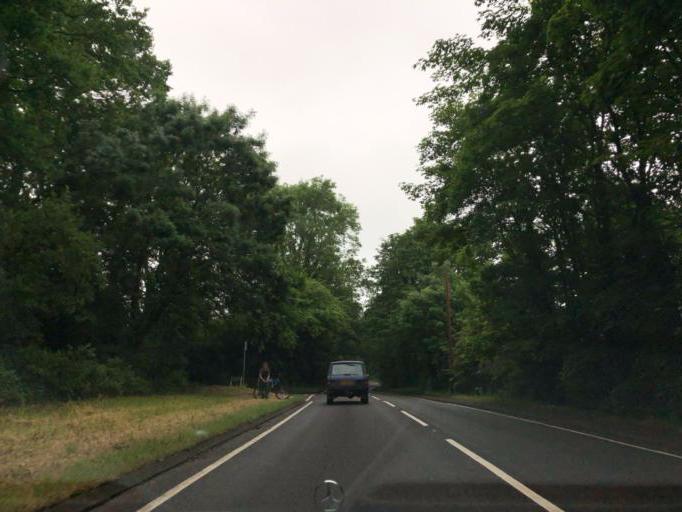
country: GB
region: England
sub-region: Warwickshire
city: Wroxall
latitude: 52.3220
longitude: -1.6659
